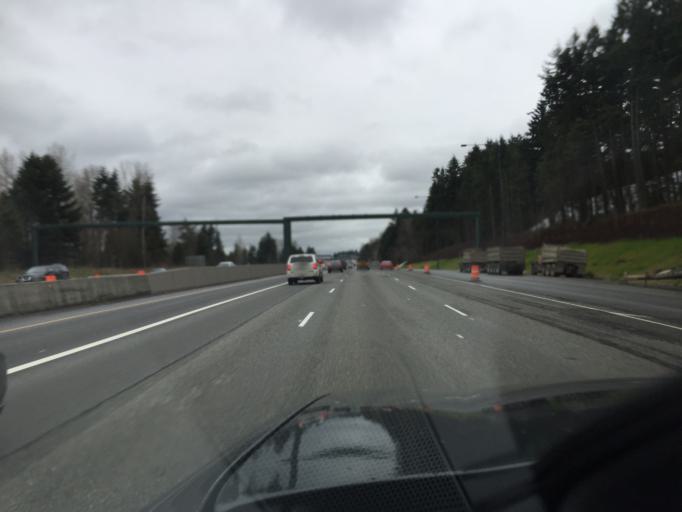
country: US
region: Washington
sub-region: King County
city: Kingsgate
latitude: 47.7297
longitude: -122.1887
